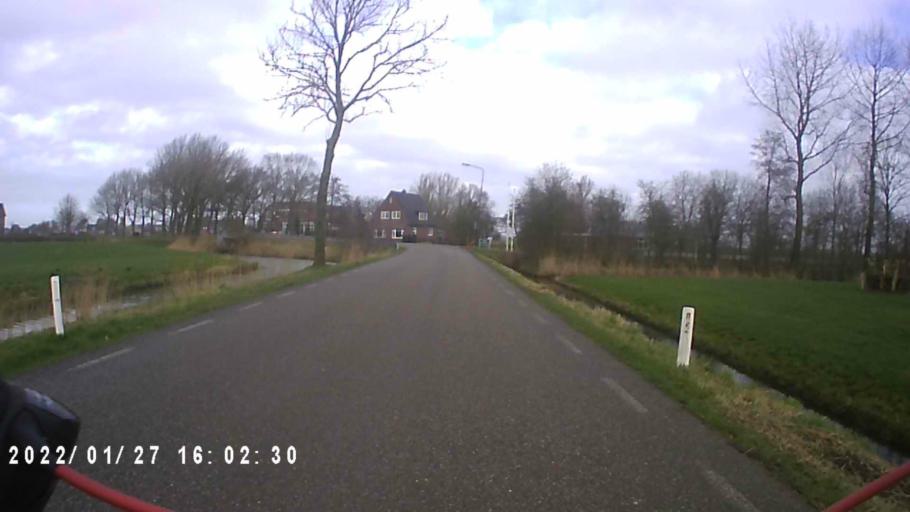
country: NL
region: Friesland
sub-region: Gemeente Dongeradeel
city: Anjum
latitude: 53.3753
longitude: 6.0893
